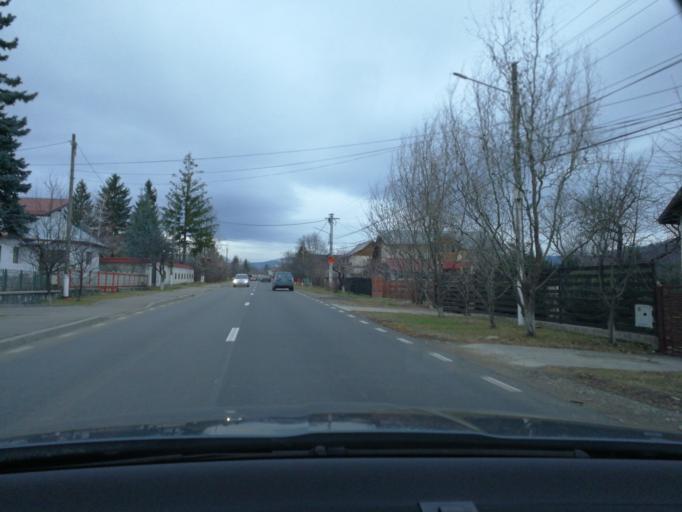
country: RO
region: Prahova
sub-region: Oras Breaza
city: Breaza de Jos
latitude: 45.1639
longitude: 25.6838
